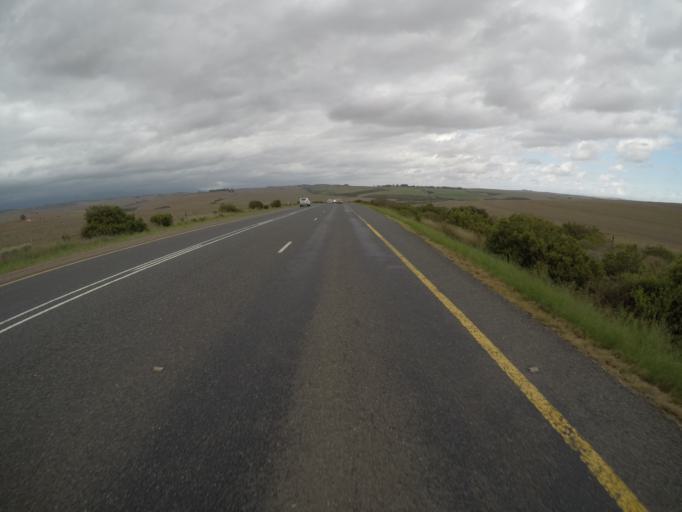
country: ZA
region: Western Cape
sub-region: Overberg District Municipality
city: Swellendam
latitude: -34.1037
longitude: 20.7516
